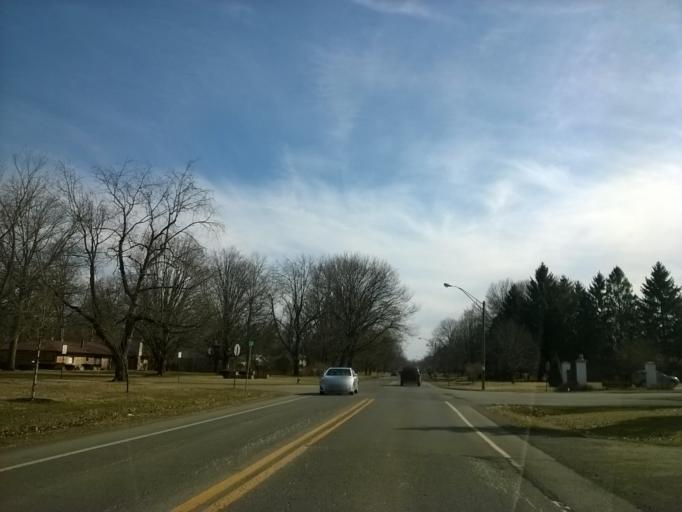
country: US
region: Indiana
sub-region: Marion County
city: Meridian Hills
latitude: 39.8466
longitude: -86.2119
